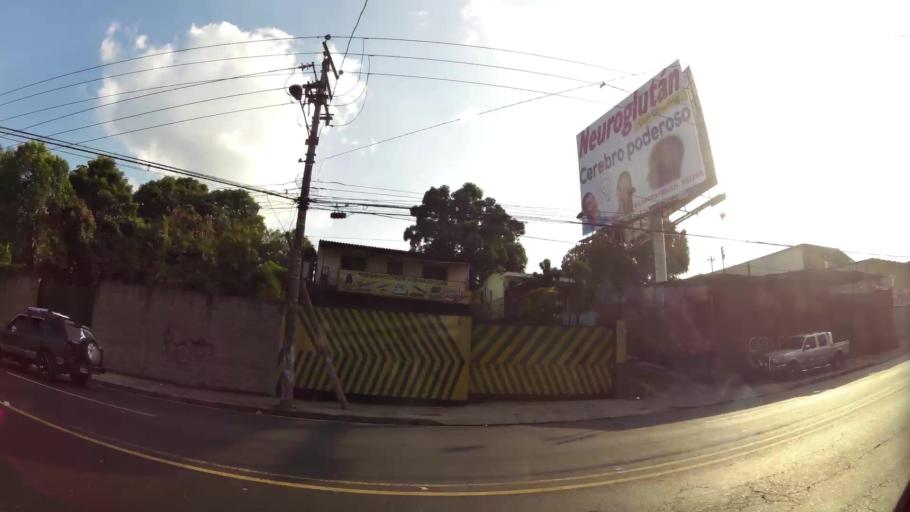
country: SV
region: San Salvador
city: San Salvador
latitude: 13.6953
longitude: -89.1779
